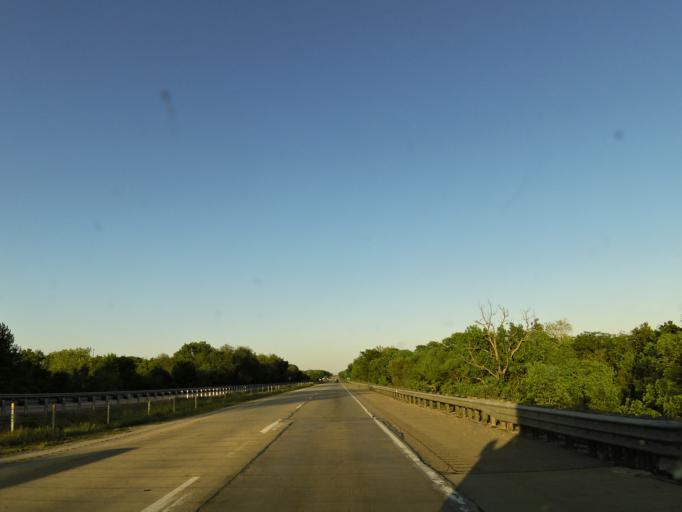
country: US
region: Illinois
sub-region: Vermilion County
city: Danville
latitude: 40.1143
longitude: -87.6003
